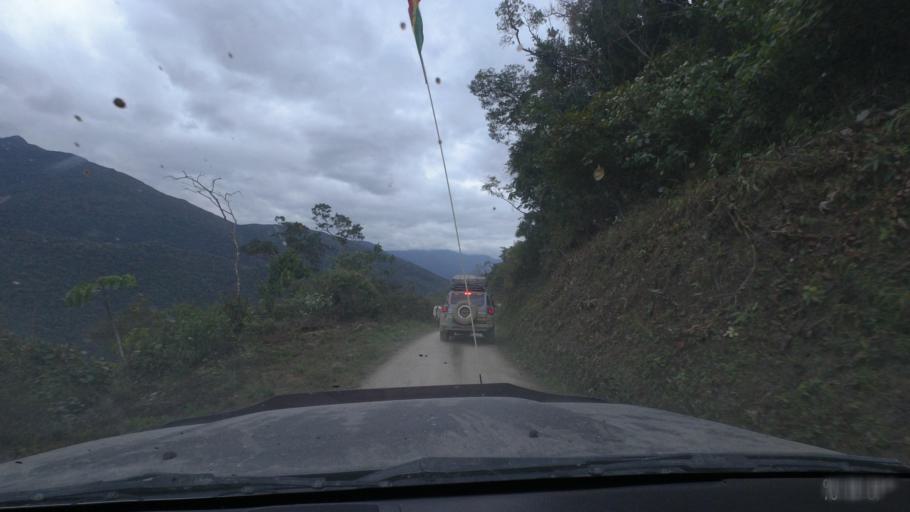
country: BO
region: La Paz
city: Quime
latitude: -16.5222
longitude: -66.7692
